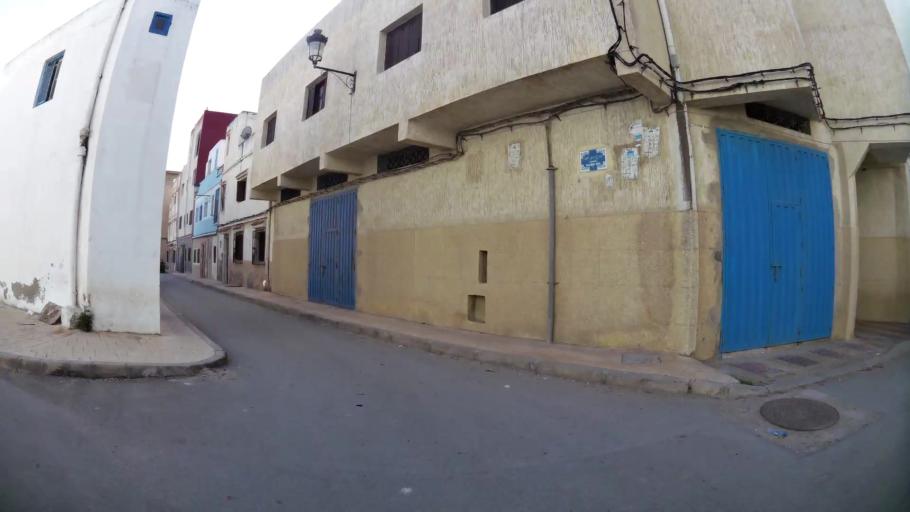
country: MA
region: Tanger-Tetouan
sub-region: Tetouan
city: Martil
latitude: 35.6118
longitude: -5.2806
